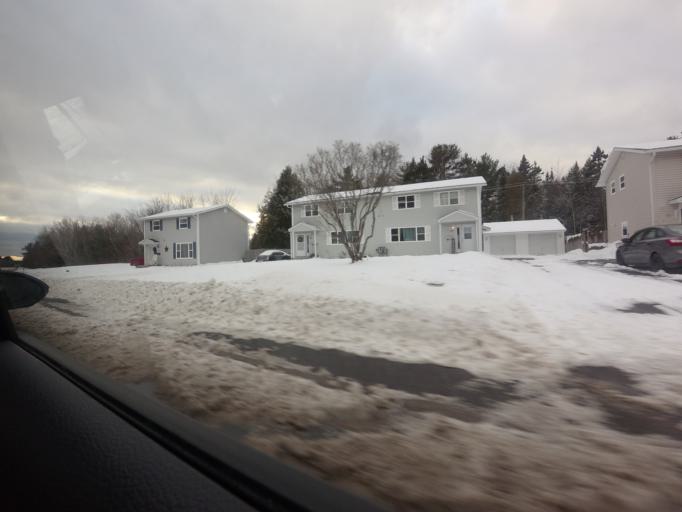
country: CA
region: New Brunswick
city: Oromocto
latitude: 45.8435
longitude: -66.4903
